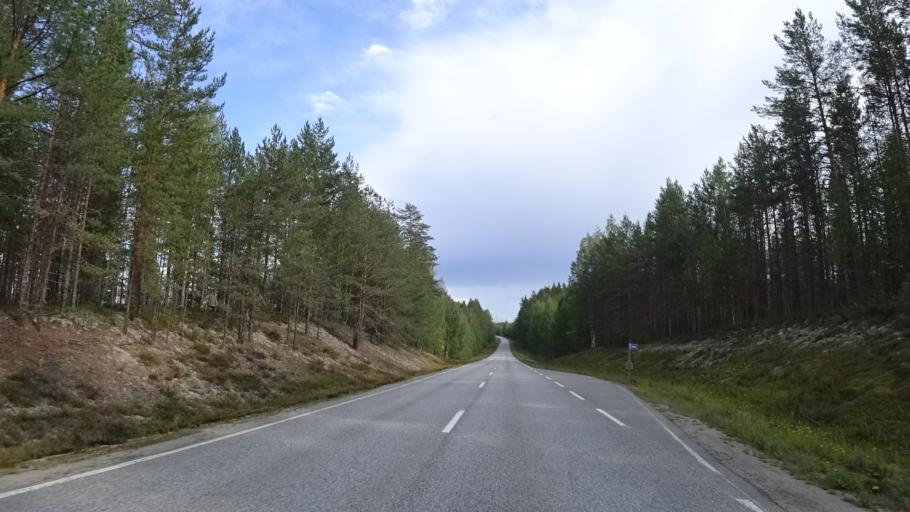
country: FI
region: North Karelia
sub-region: Joensuu
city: Ilomantsi
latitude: 62.6262
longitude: 31.1054
